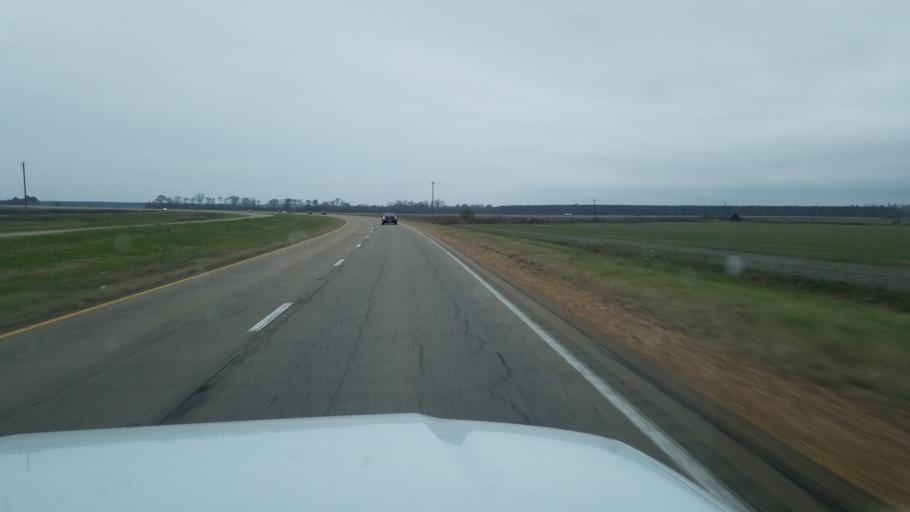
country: US
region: Mississippi
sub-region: Chickasaw County
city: Okolona
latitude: 33.9369
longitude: -88.7342
